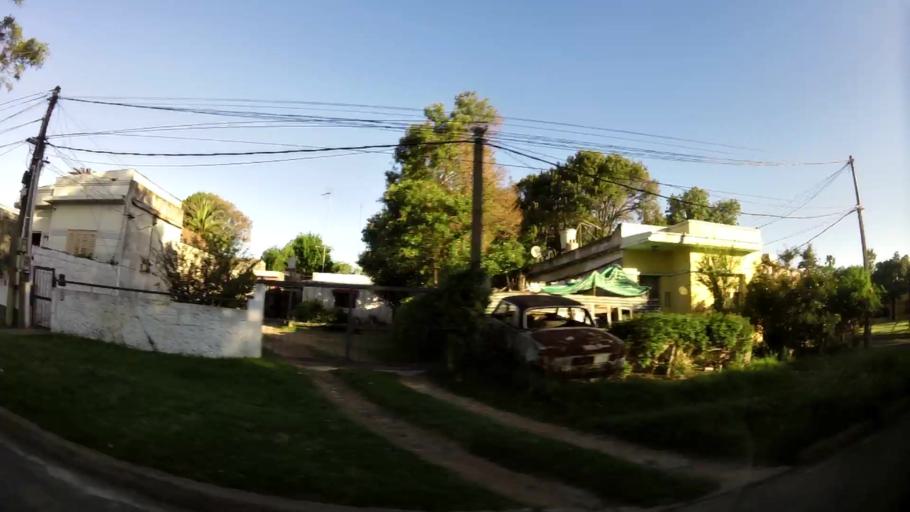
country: UY
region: Montevideo
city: Montevideo
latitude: -34.8423
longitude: -56.2115
